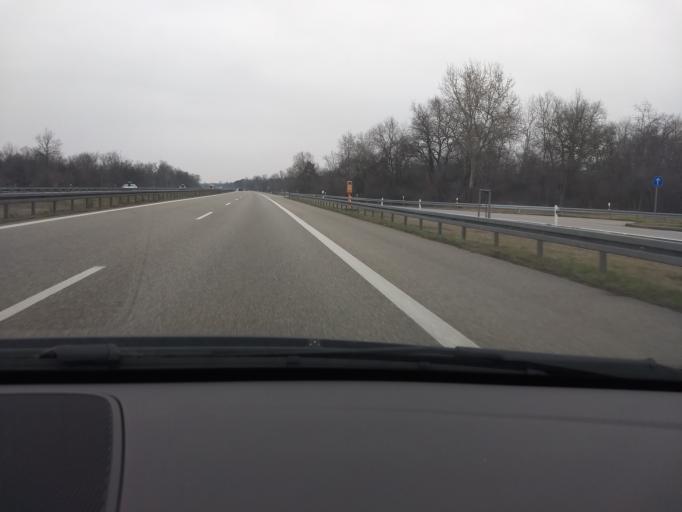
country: DE
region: Baden-Wuerttemberg
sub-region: Freiburg Region
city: Neuenburg am Rhein
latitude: 47.8305
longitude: 7.5635
